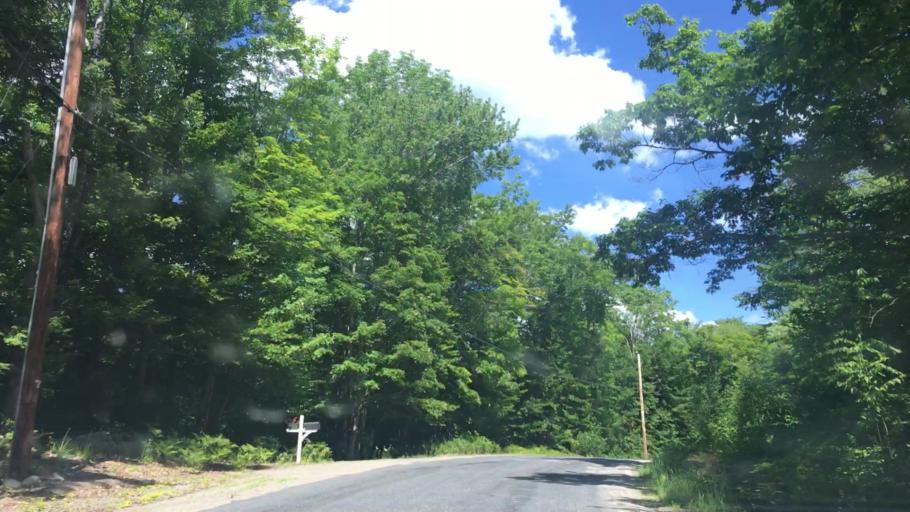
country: US
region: Maine
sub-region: Franklin County
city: Chesterville
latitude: 44.5586
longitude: -70.1225
